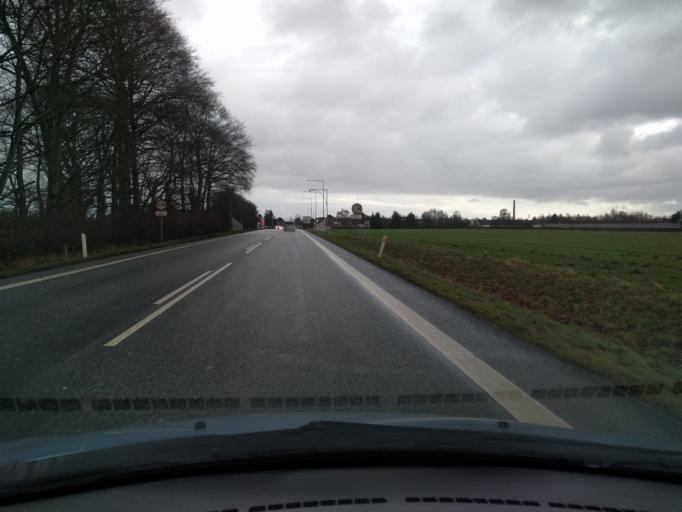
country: DK
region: South Denmark
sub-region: Kerteminde Kommune
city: Langeskov
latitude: 55.3645
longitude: 10.5815
